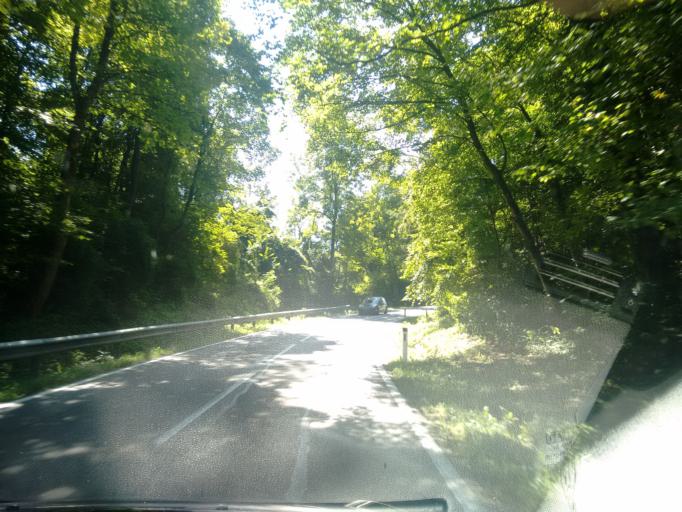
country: DE
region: Bavaria
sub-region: Lower Bavaria
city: Julbach
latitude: 48.2089
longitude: 12.9686
